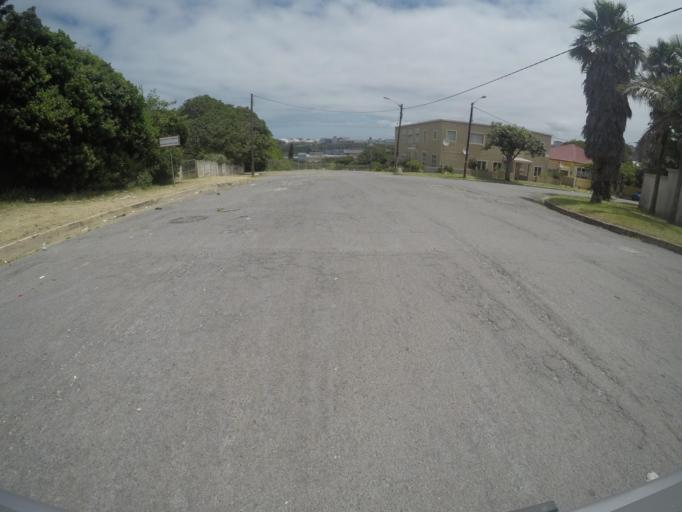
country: ZA
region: Eastern Cape
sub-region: Buffalo City Metropolitan Municipality
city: East London
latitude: -33.0221
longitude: 27.9105
